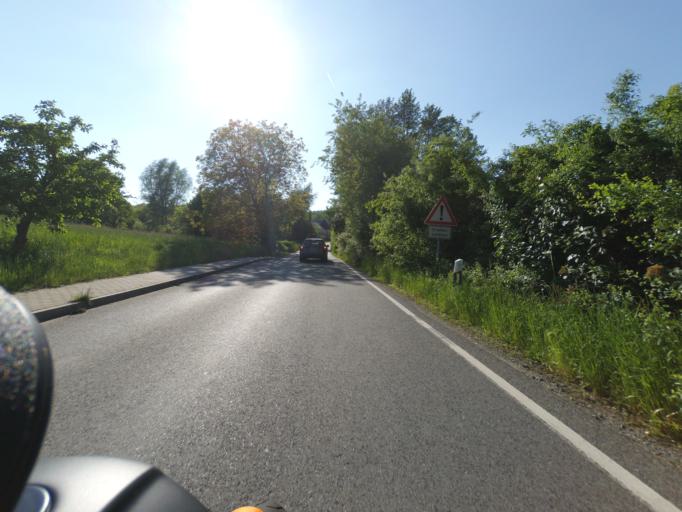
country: DE
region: Saxony
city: Bannewitz
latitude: 50.9707
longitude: 13.7017
